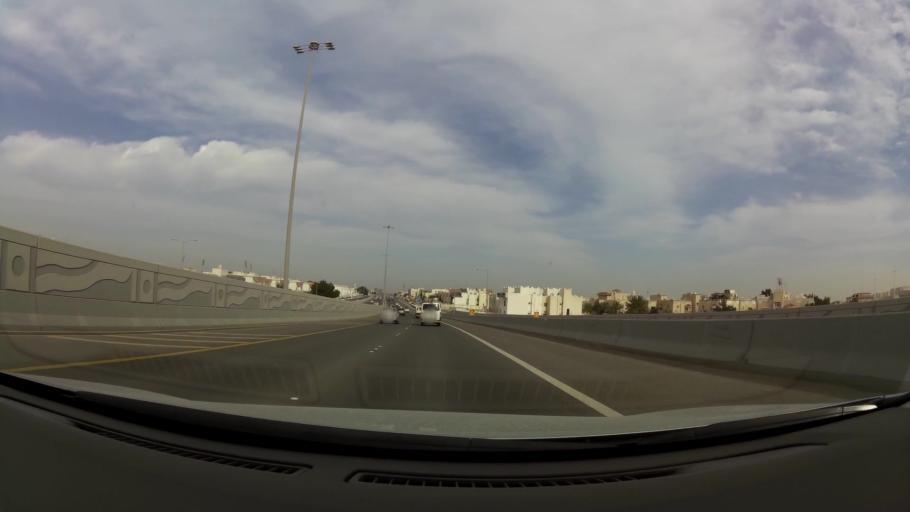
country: QA
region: Baladiyat ad Dawhah
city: Doha
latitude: 25.2544
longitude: 51.5085
